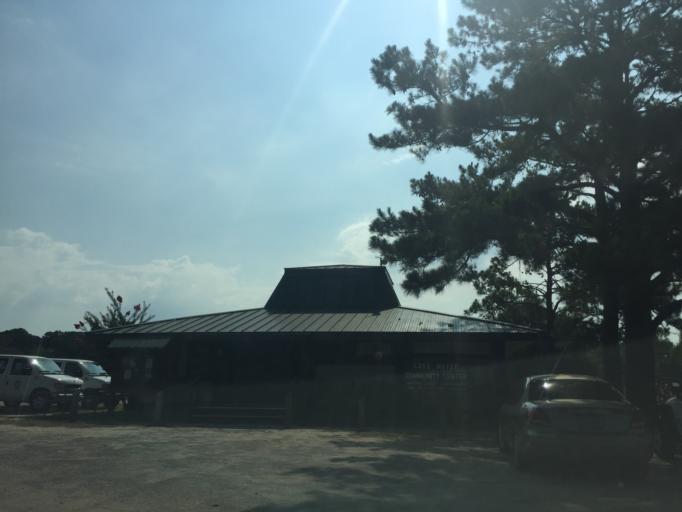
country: US
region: Georgia
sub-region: Chatham County
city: Isle of Hope
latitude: 31.9924
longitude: -81.0877
